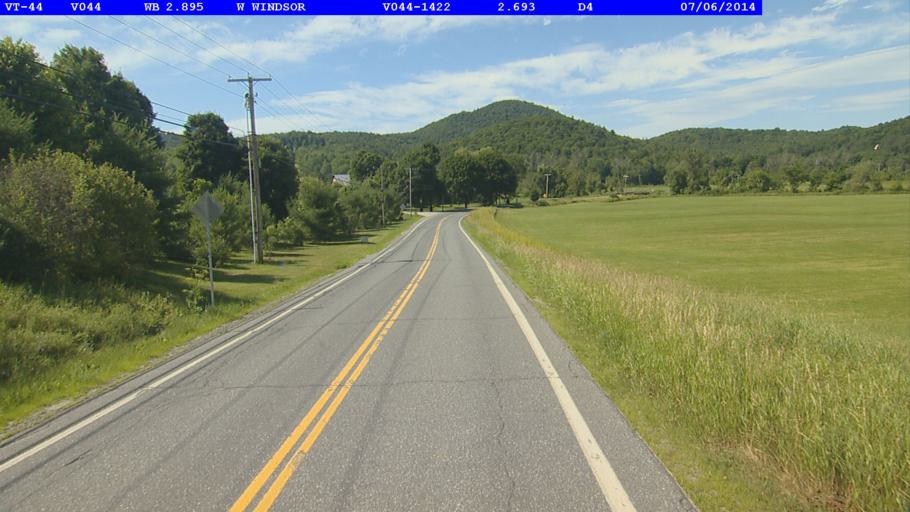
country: US
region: Vermont
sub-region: Windsor County
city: Windsor
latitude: 43.4555
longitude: -72.4915
